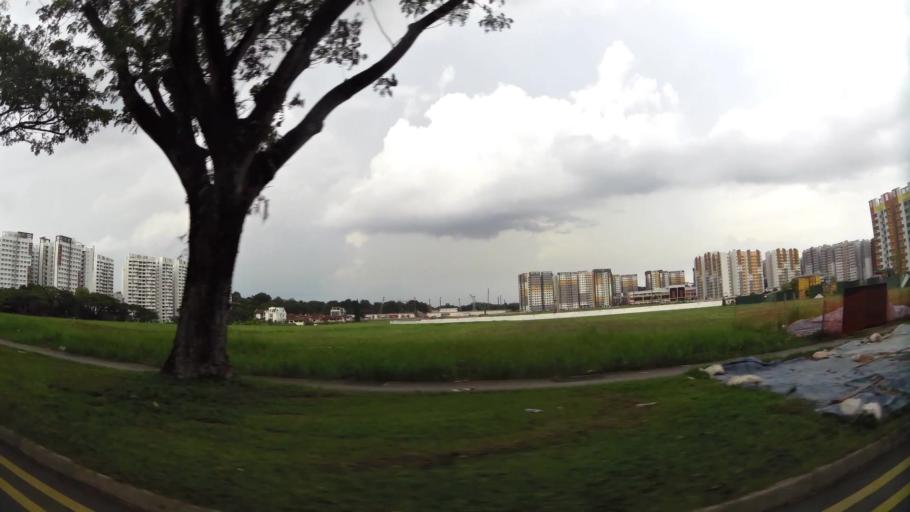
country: MY
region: Johor
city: Kampung Pasir Gudang Baru
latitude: 1.4472
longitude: 103.8274
